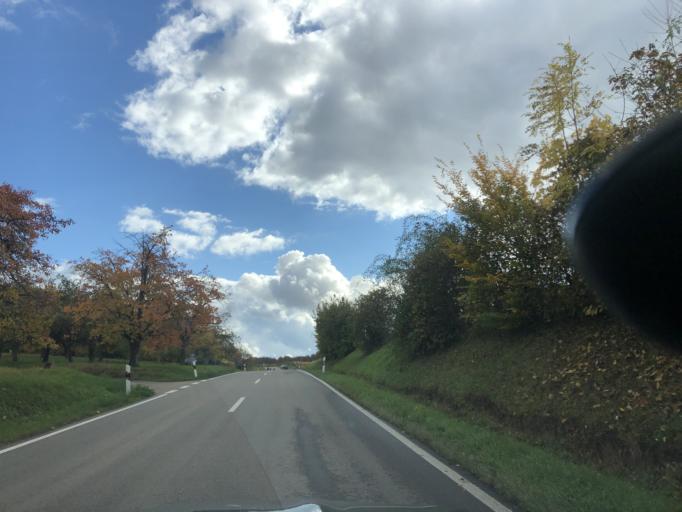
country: DE
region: Baden-Wuerttemberg
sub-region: Regierungsbezirk Stuttgart
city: Baltmannsweiler
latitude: 48.7895
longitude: 9.4190
